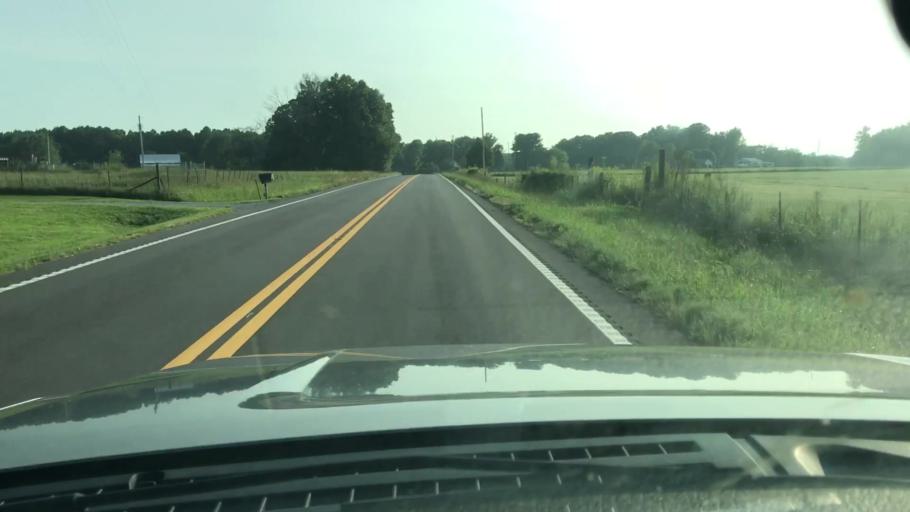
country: US
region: Tennessee
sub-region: Sumner County
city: Portland
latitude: 36.5659
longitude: -86.3840
